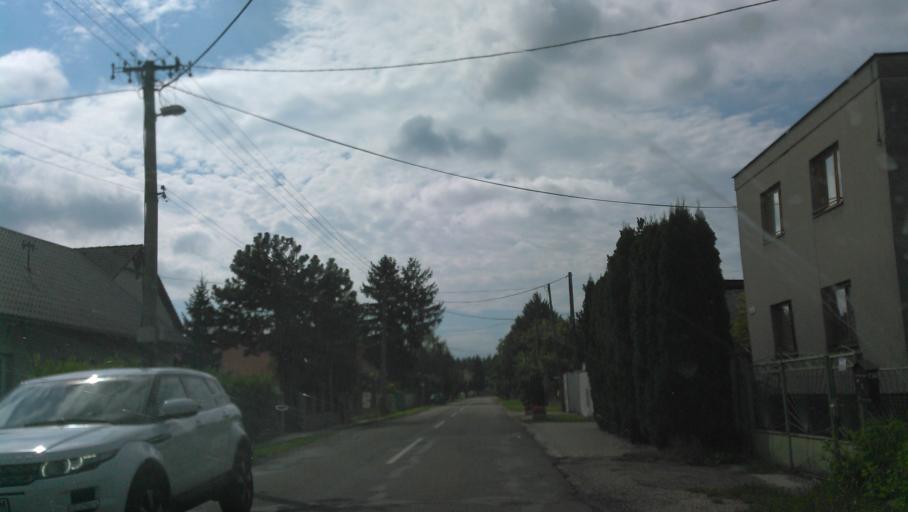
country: SK
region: Bratislavsky
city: Dunajska Luzna
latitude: 48.1675
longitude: 17.2776
